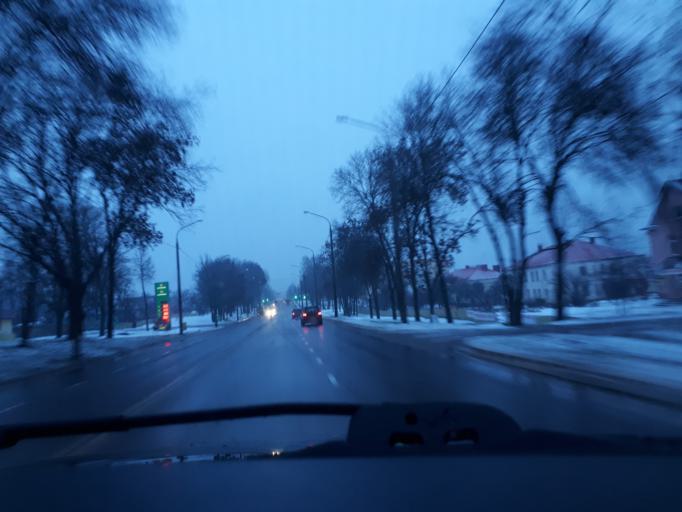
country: BY
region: Vitebsk
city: Vitebsk
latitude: 55.2227
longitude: 30.1179
